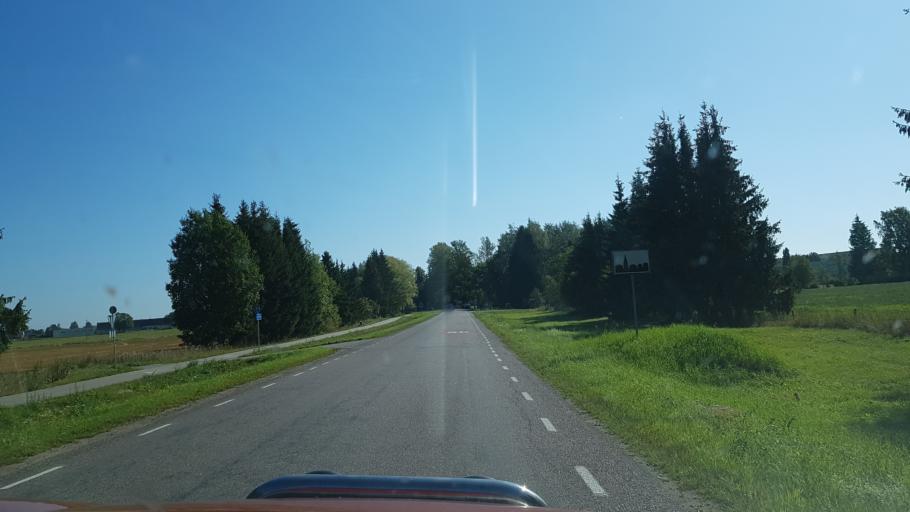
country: EE
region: Tartu
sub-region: Tartu linn
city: Tartu
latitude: 58.3568
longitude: 26.8683
